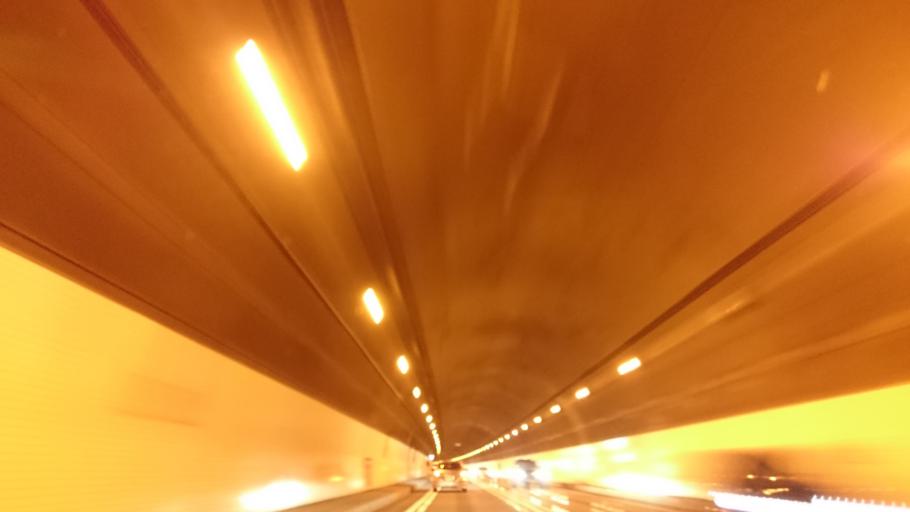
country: JP
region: Gifu
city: Gujo
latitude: 35.9185
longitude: 136.8711
